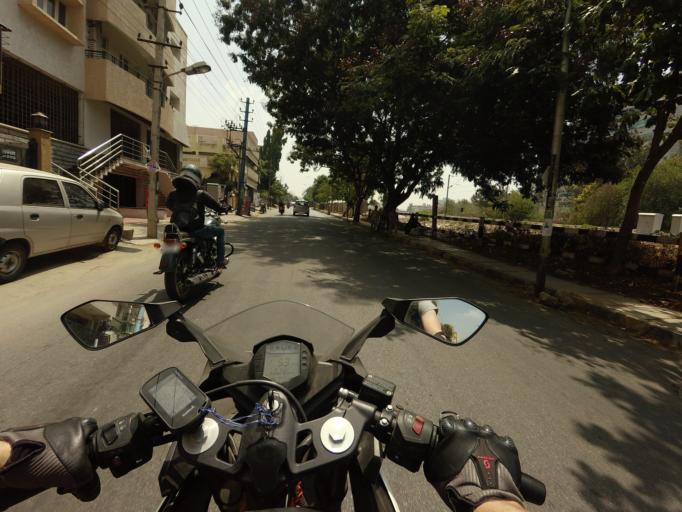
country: IN
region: Karnataka
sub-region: Bangalore Urban
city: Bangalore
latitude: 12.9955
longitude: 77.6600
